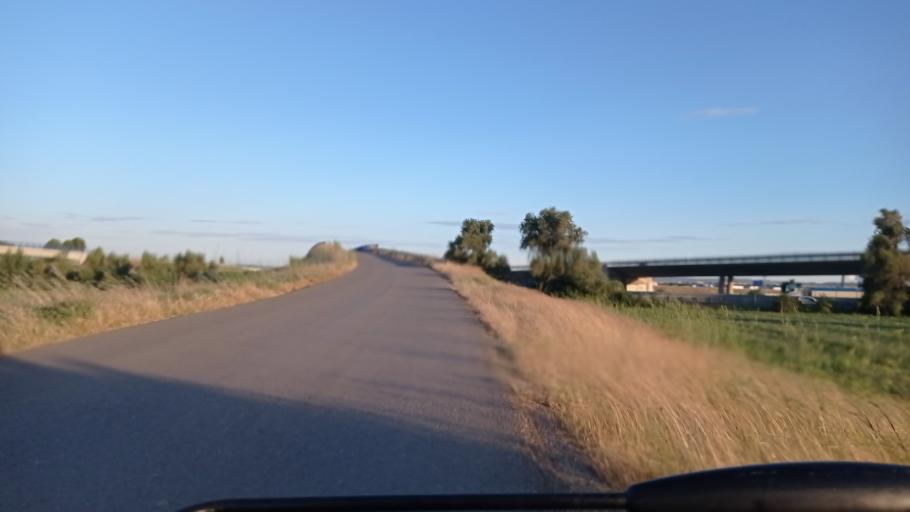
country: ES
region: Aragon
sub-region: Provincia de Zaragoza
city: Oliver-Valdefierro, Oliver, Valdefierro
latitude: 41.6786
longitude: -0.9312
